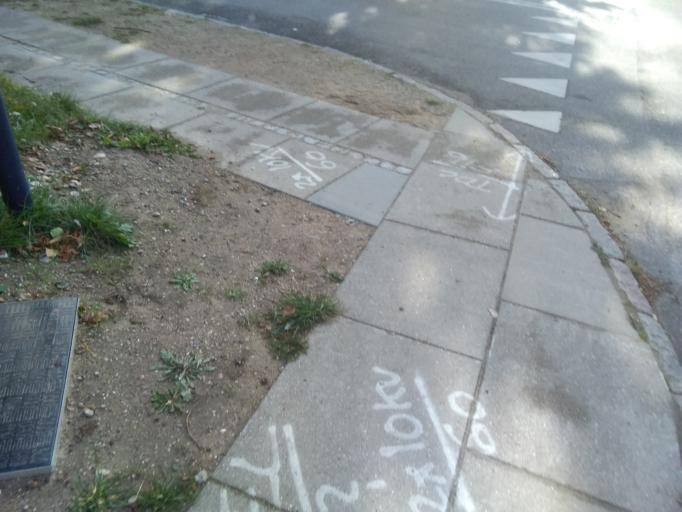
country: DK
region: Capital Region
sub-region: Kobenhavn
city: Vanlose
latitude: 55.6974
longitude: 12.4885
